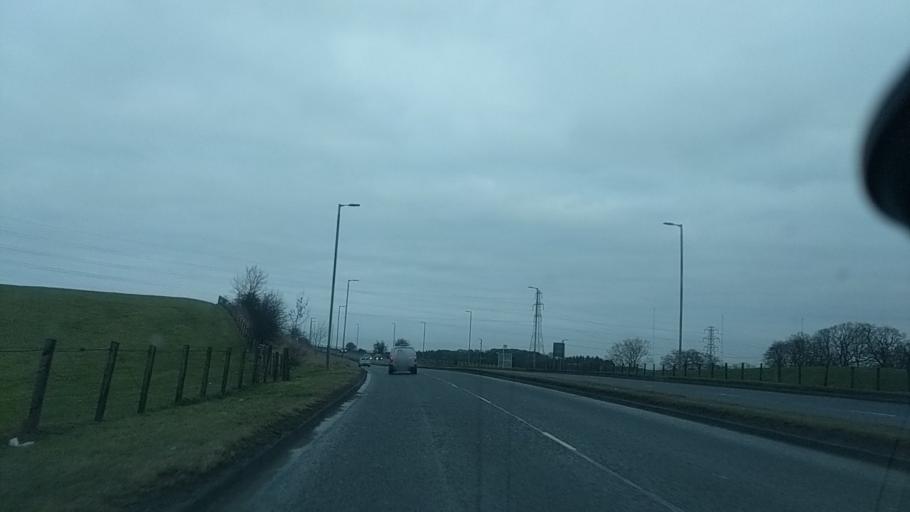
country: GB
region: Scotland
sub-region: South Lanarkshire
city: East Kilbride
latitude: 55.7884
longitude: -4.1664
